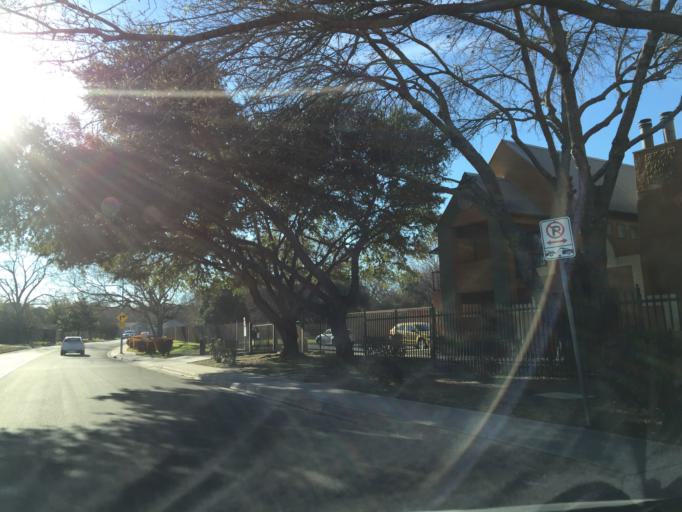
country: US
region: Texas
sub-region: Travis County
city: Onion Creek
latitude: 30.2039
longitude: -97.7844
